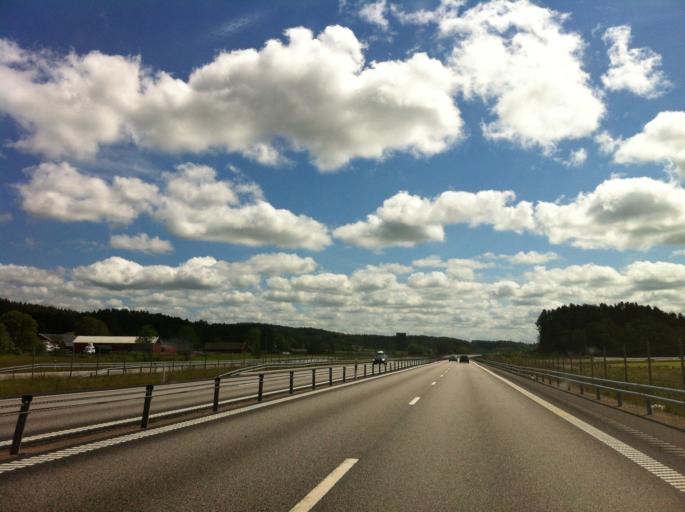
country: SE
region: Vaestra Goetaland
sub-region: Lilla Edets Kommun
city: Lilla Edet
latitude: 58.0897
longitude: 12.1557
